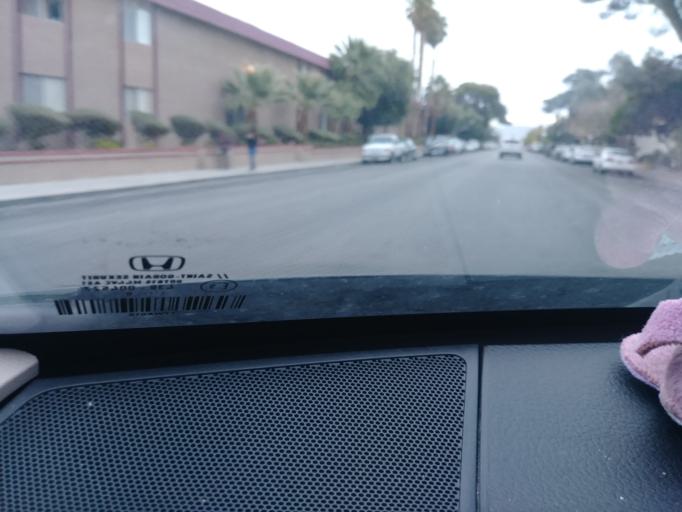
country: US
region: Nevada
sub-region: Clark County
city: Spring Valley
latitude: 36.1768
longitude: -115.2232
